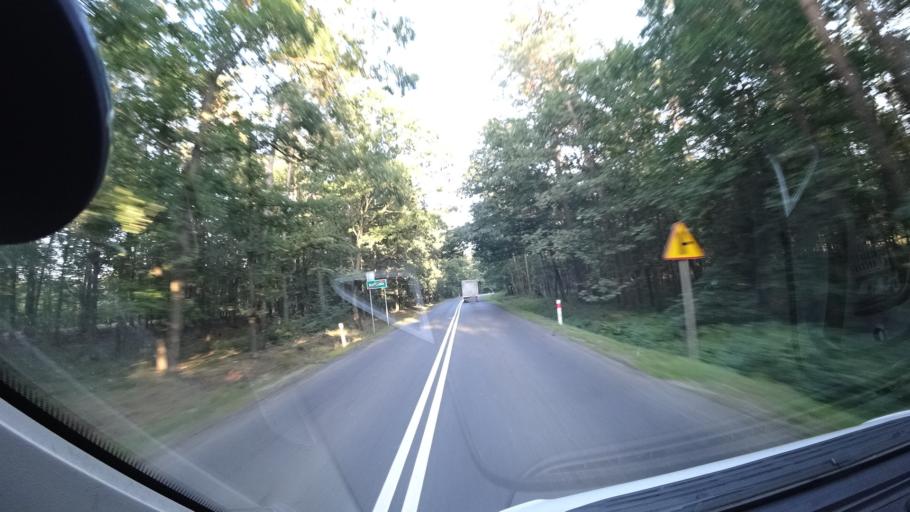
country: PL
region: Silesian Voivodeship
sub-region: Powiat gliwicki
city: Rudziniec
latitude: 50.2761
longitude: 18.3768
